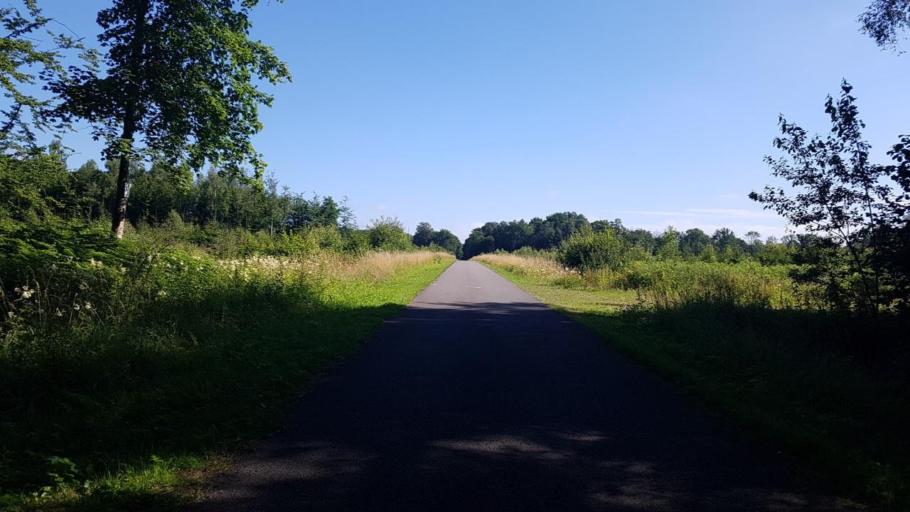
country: FR
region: Nord-Pas-de-Calais
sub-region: Departement du Nord
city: Anor
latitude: 49.9618
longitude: 4.1117
